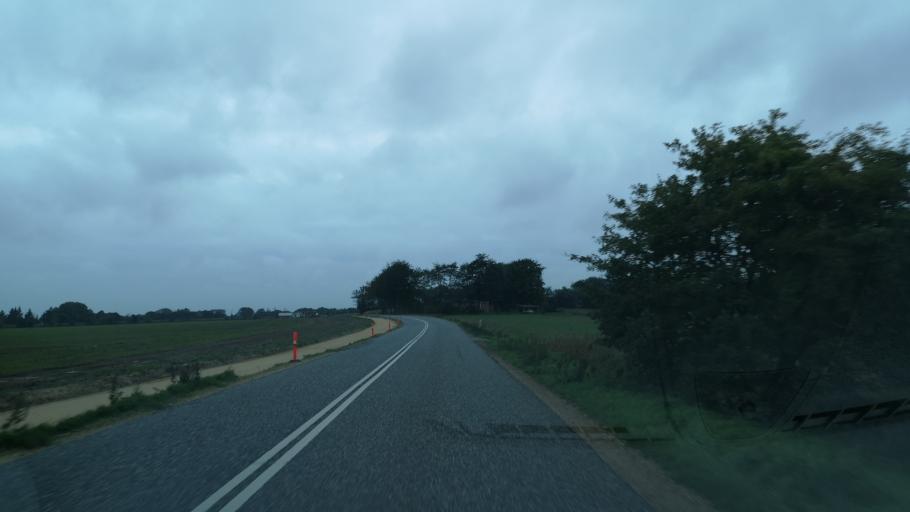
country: DK
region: Central Jutland
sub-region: Ringkobing-Skjern Kommune
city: Videbaek
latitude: 56.0546
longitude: 8.6364
